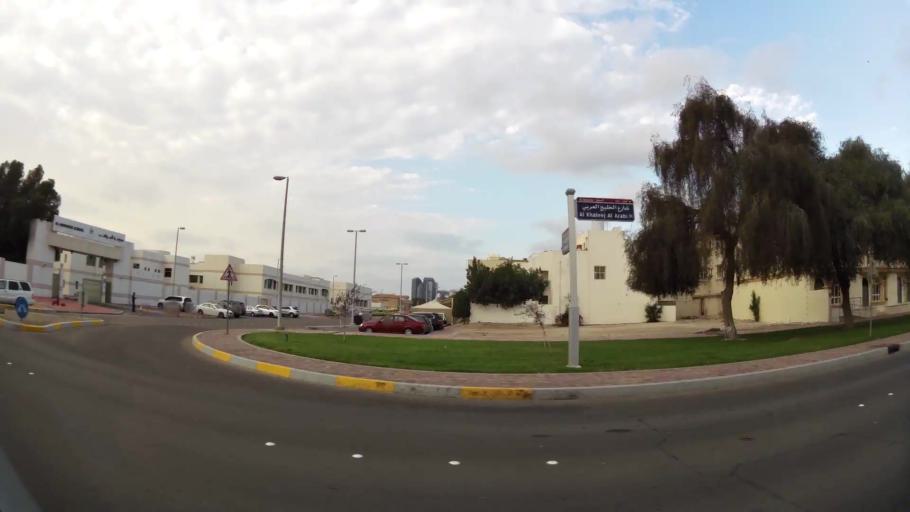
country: AE
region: Abu Dhabi
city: Abu Dhabi
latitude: 24.4639
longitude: 54.3480
